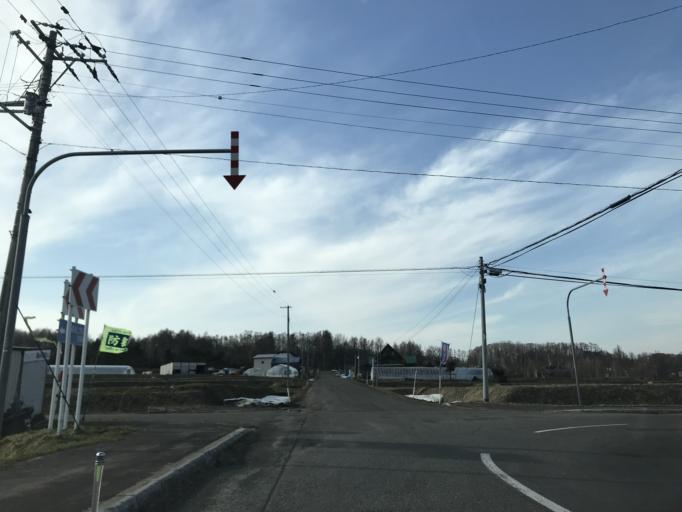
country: JP
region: Hokkaido
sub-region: Asahikawa-shi
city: Asahikawa
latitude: 43.7053
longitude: 142.3443
